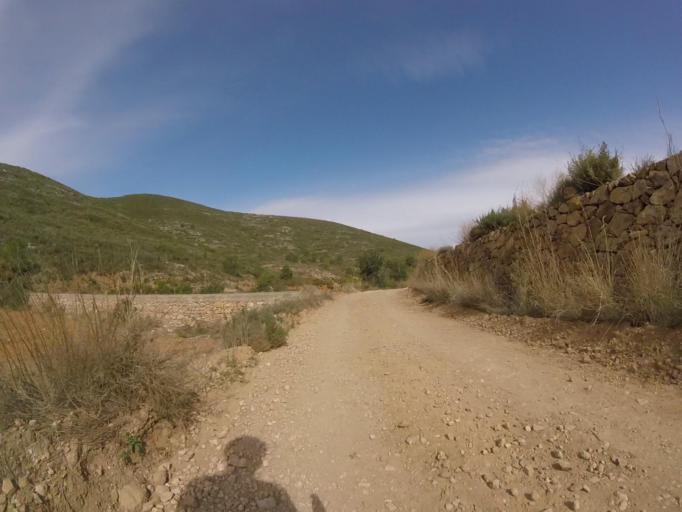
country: ES
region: Valencia
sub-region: Provincia de Castello
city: Torreblanca
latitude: 40.1975
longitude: 0.1558
